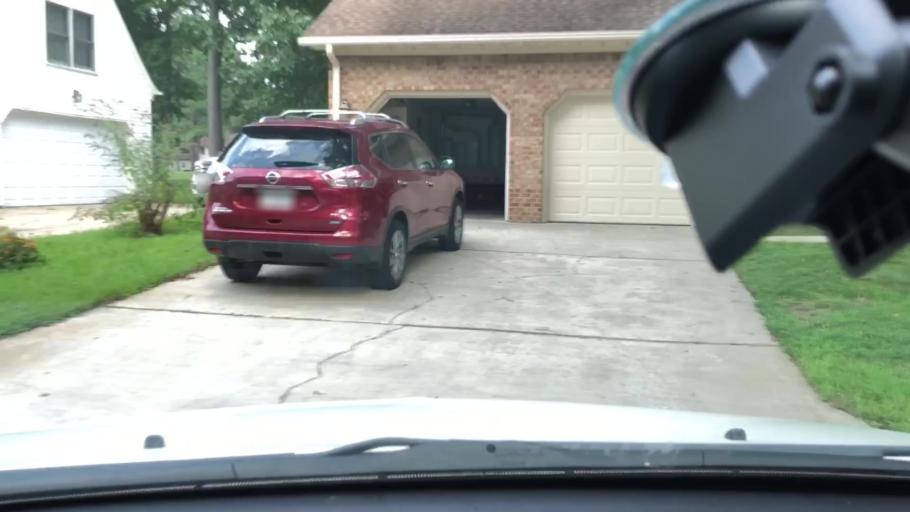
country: US
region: Virginia
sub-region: City of Chesapeake
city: Chesapeake
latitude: 36.7078
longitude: -76.2910
